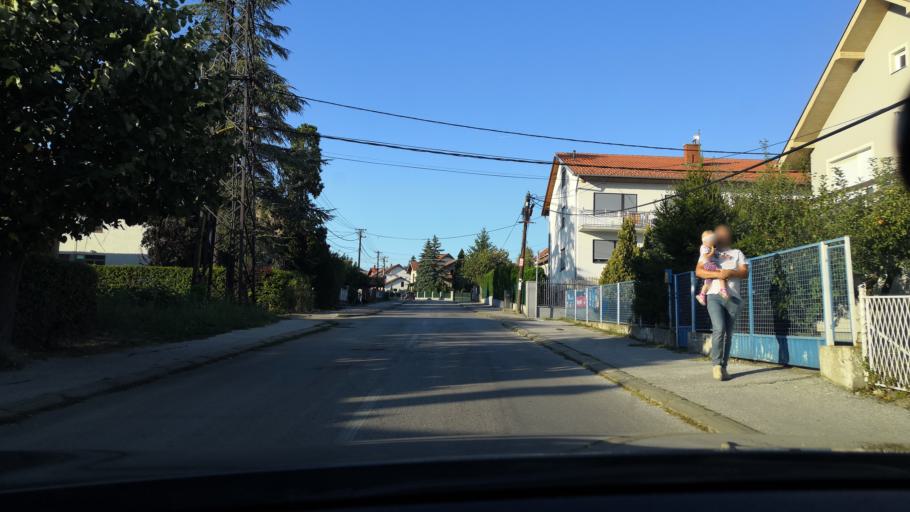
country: RS
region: Central Serbia
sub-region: Sumadijski Okrug
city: Arangelovac
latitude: 44.3161
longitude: 20.5590
